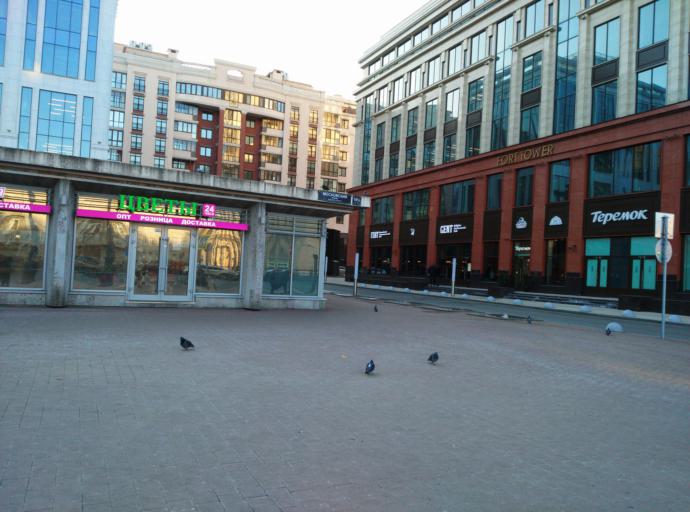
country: RU
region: St.-Petersburg
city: Admiralteisky
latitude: 59.8793
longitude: 30.3191
